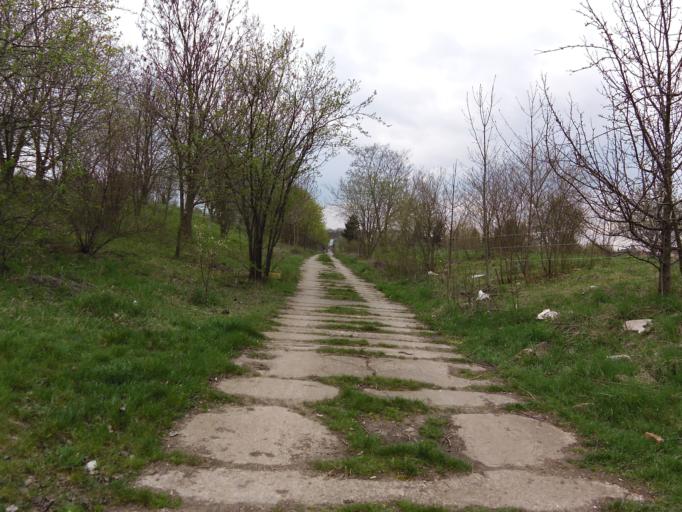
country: DE
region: Thuringia
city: Gotha
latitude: 50.9593
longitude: 10.7015
